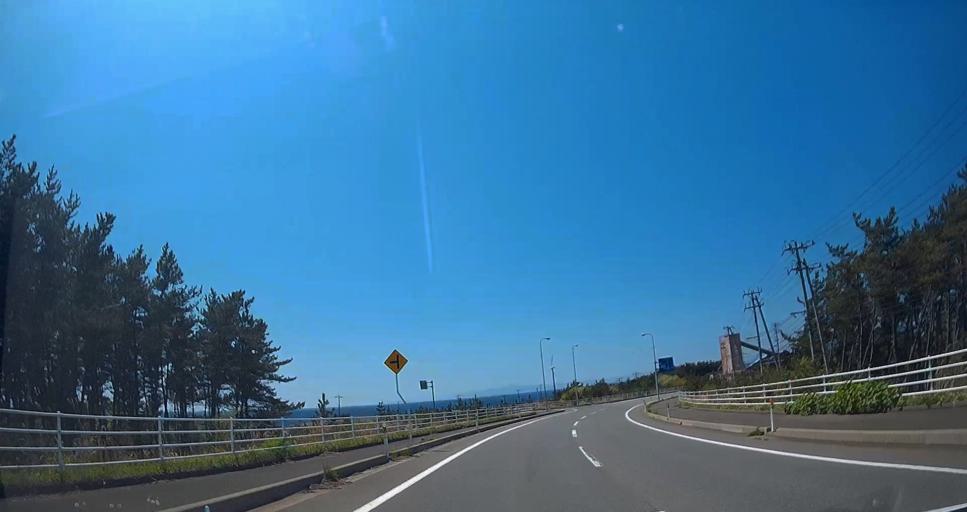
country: JP
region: Hokkaido
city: Hakodate
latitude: 41.5203
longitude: 140.9091
